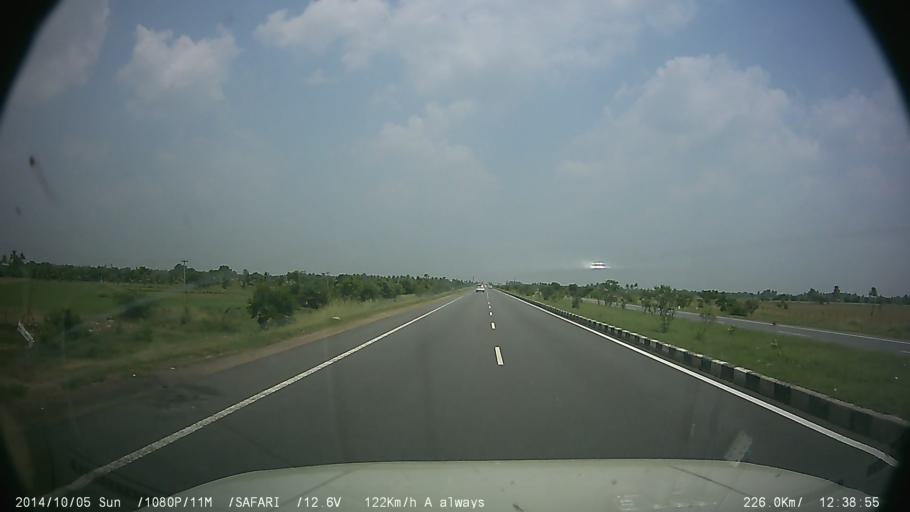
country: IN
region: Tamil Nadu
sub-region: Cuddalore
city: Vriddhachalam
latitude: 11.6795
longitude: 79.2975
